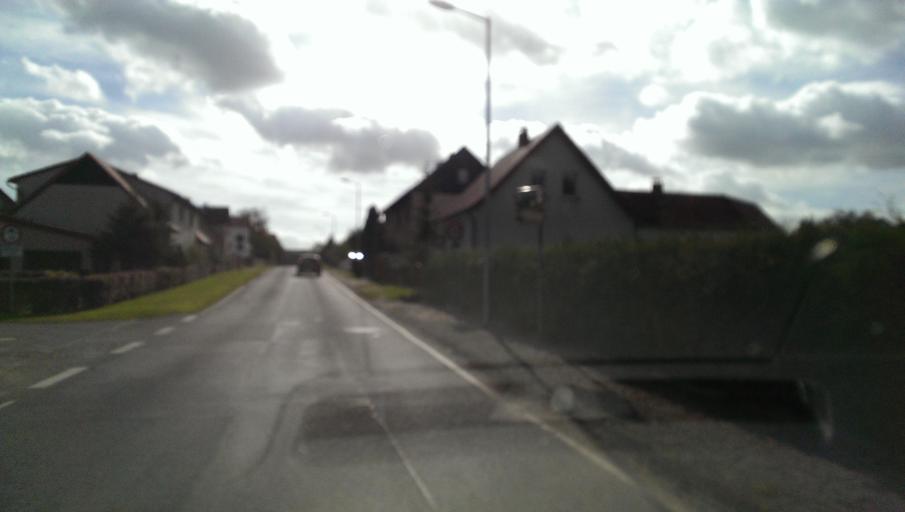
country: DE
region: Brandenburg
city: Lauchhammer
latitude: 51.5171
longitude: 13.7061
